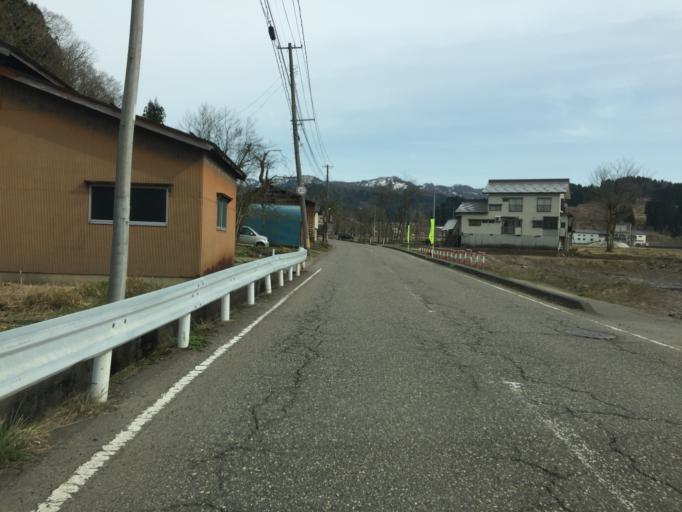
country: JP
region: Niigata
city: Tochio-honcho
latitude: 37.4502
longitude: 139.0146
